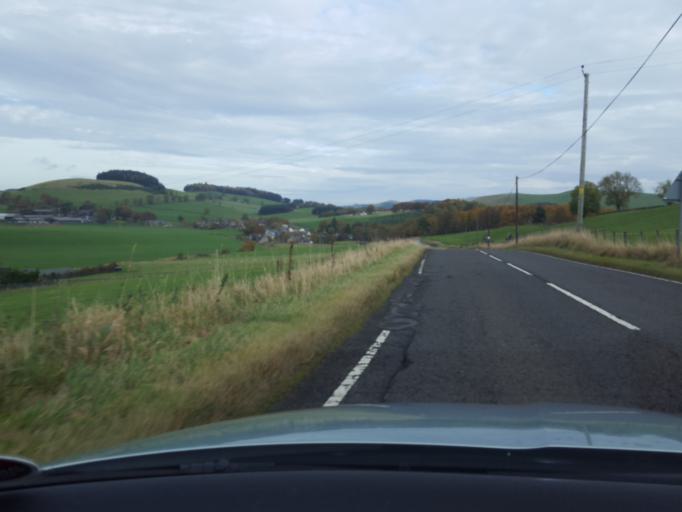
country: GB
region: Scotland
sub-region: The Scottish Borders
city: West Linton
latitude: 55.6885
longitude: -3.3918
